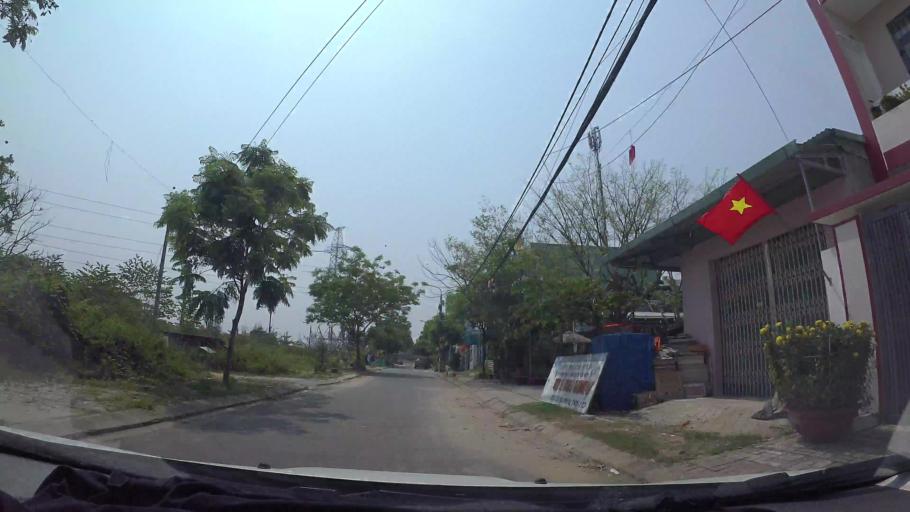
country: VN
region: Da Nang
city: Cam Le
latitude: 15.9990
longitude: 108.2078
